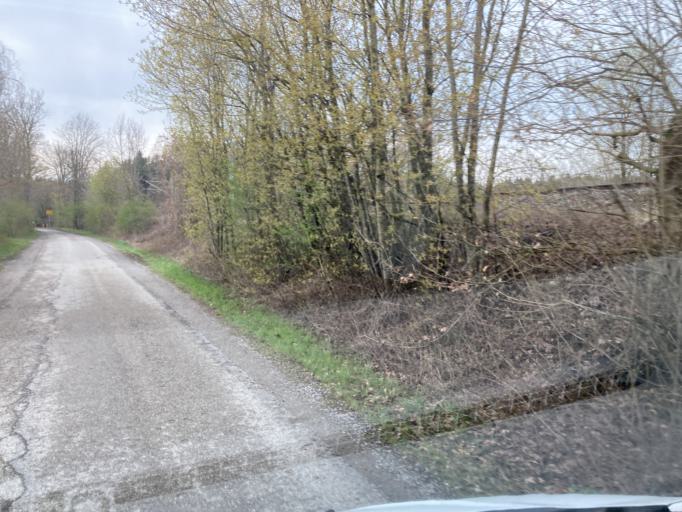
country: DE
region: Bavaria
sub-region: Upper Bavaria
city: Grafing bei Munchen
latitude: 48.0362
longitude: 11.9458
